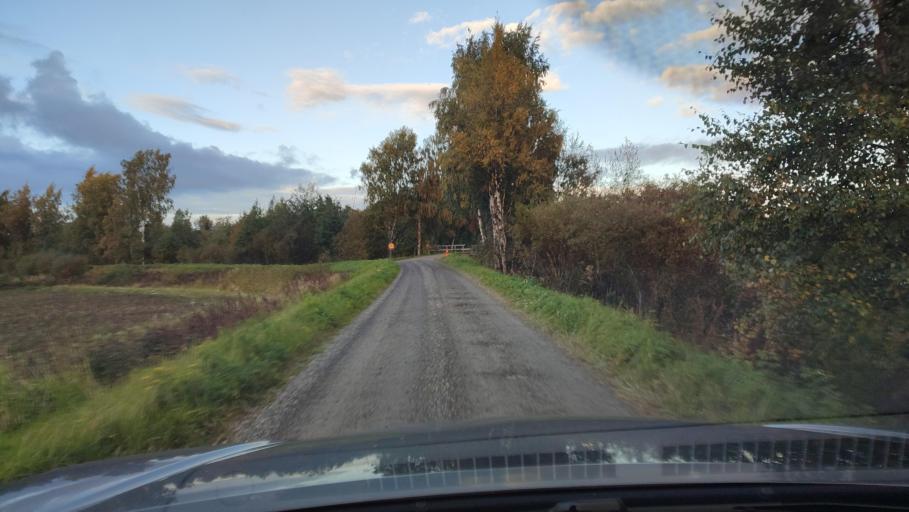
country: FI
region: Ostrobothnia
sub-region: Sydosterbotten
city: Kristinestad
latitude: 62.2320
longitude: 21.4500
